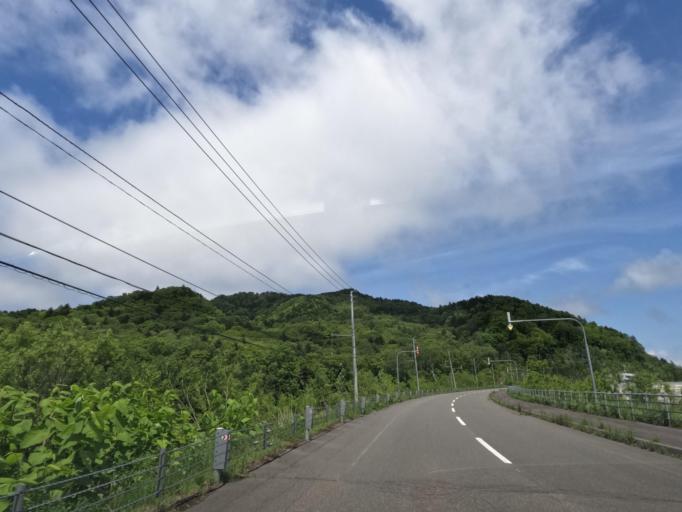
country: JP
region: Hokkaido
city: Tobetsu
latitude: 43.3177
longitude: 141.5585
